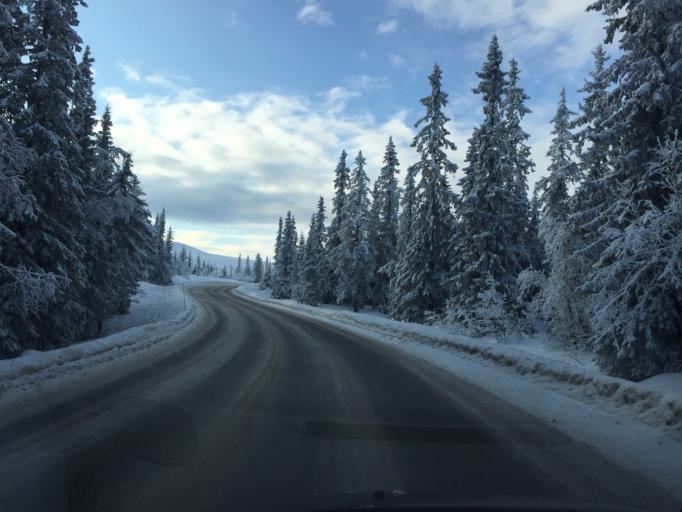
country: NO
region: Hedmark
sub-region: Trysil
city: Innbygda
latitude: 61.3354
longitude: 12.1735
